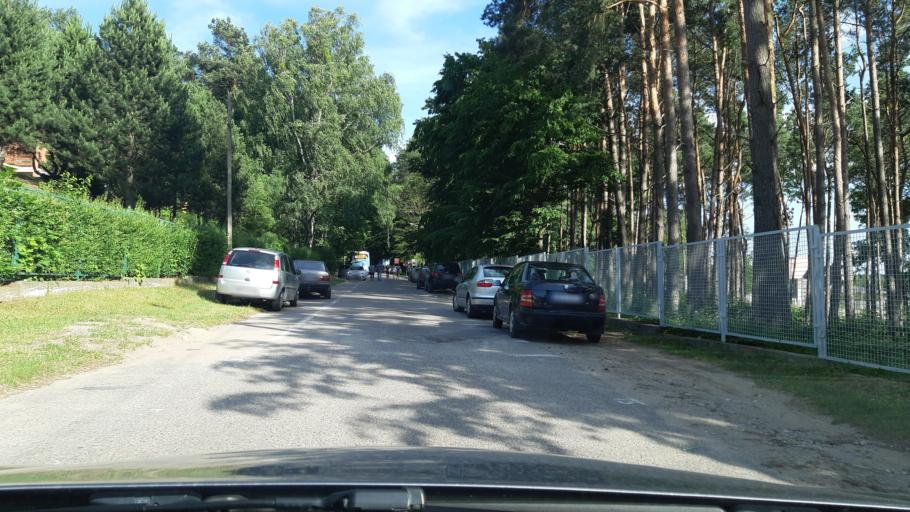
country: PL
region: Warmian-Masurian Voivodeship
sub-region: Powiat mragowski
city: Mragowo
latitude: 53.8738
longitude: 21.3210
